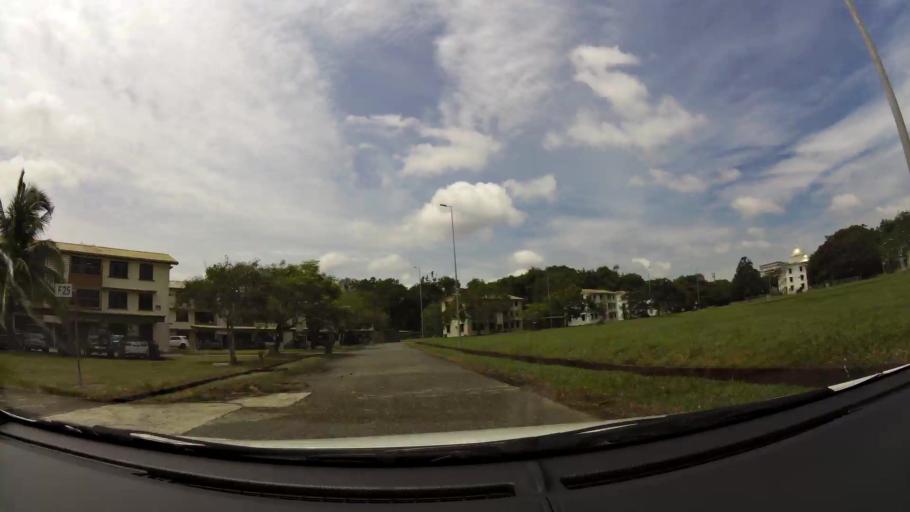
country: BN
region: Brunei and Muara
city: Bandar Seri Begawan
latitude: 4.9205
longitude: 114.9322
